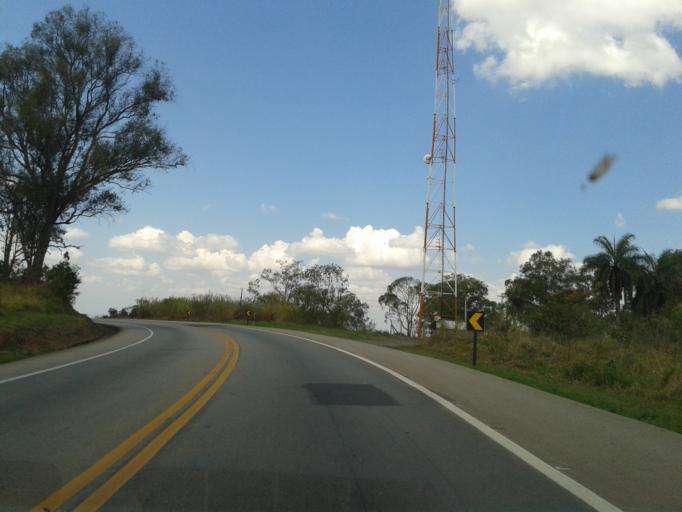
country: BR
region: Minas Gerais
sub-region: Campos Altos
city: Campos Altos
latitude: -19.7461
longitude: -45.9498
